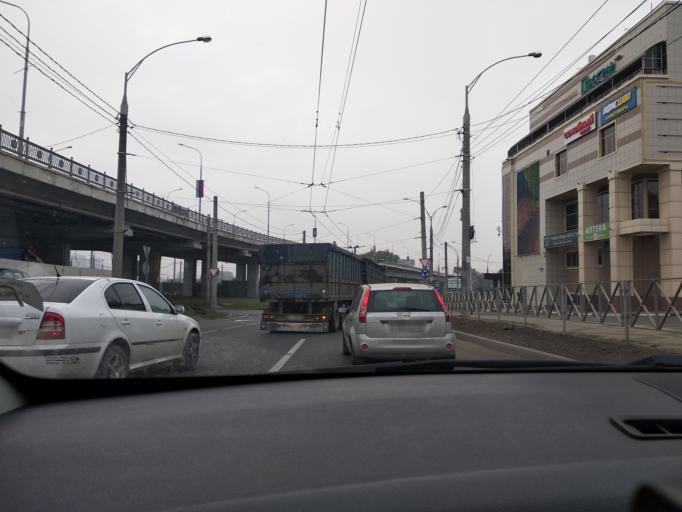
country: RU
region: Krasnodarskiy
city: Krasnodar
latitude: 45.0379
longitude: 38.9546
